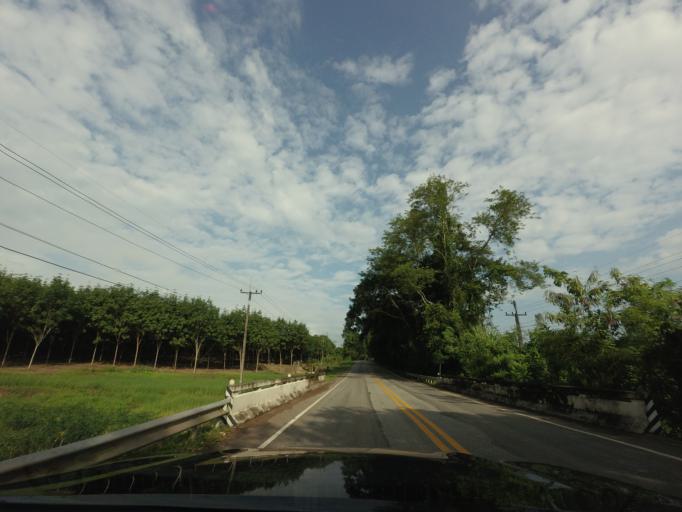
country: TH
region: Nong Khai
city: Pho Tak
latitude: 17.7983
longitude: 102.3502
